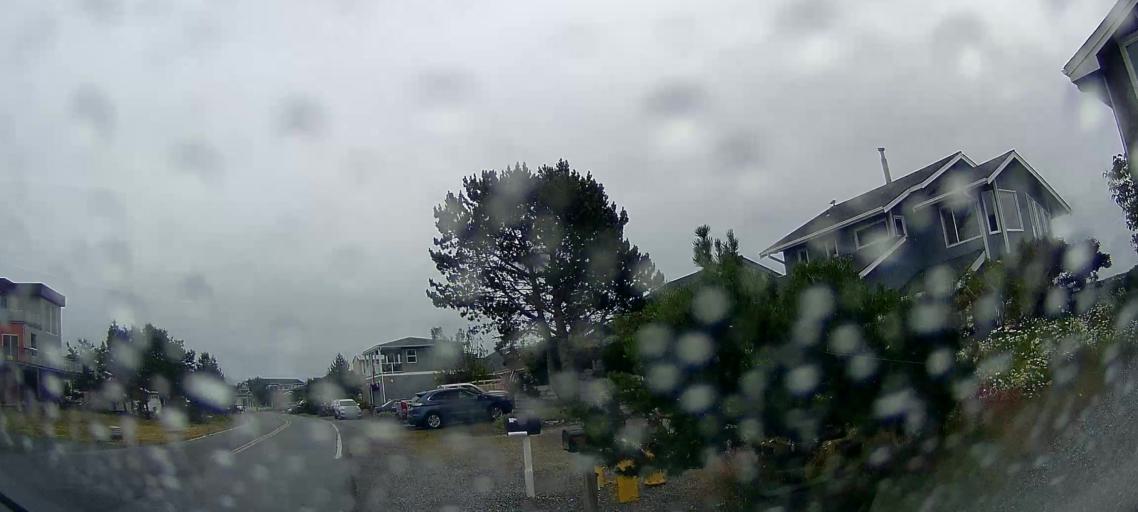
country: US
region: Washington
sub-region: Whatcom County
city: Marietta
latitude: 48.7871
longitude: -122.7046
